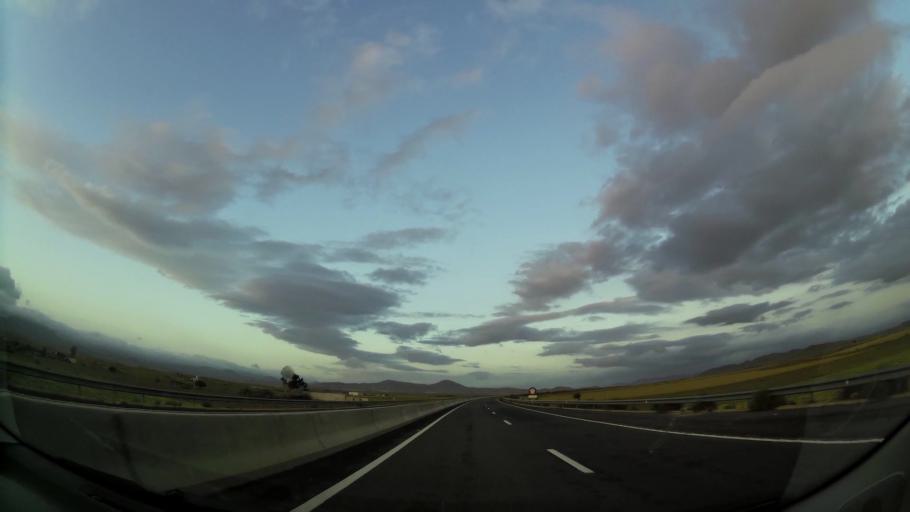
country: MA
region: Oriental
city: Taourirt
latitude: 34.6053
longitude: -2.7596
